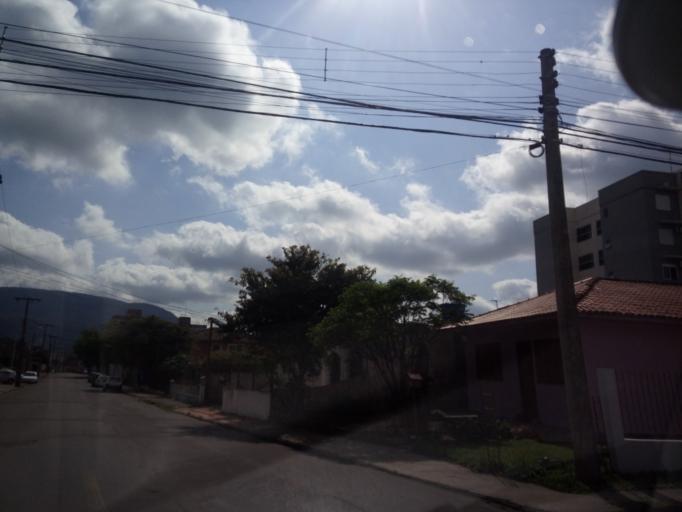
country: BR
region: Rio Grande do Sul
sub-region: Santa Maria
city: Santa Maria
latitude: -29.7016
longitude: -53.7126
